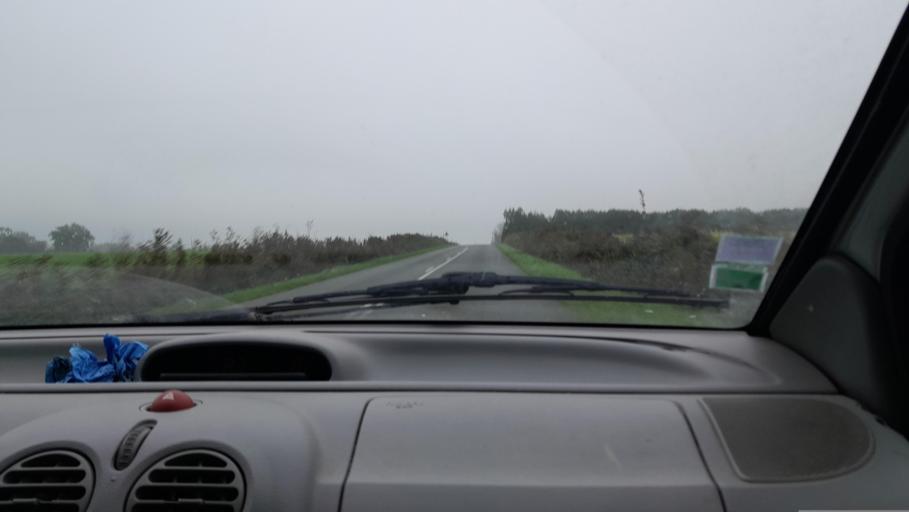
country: FR
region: Pays de la Loire
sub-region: Departement de la Mayenne
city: Loiron
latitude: 48.0229
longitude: -0.9239
